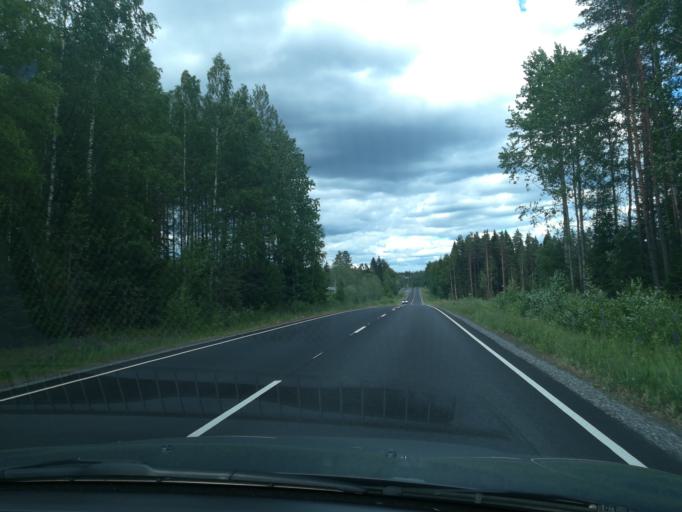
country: FI
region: Southern Savonia
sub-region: Mikkeli
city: Mikkeli
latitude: 61.6547
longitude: 27.0971
